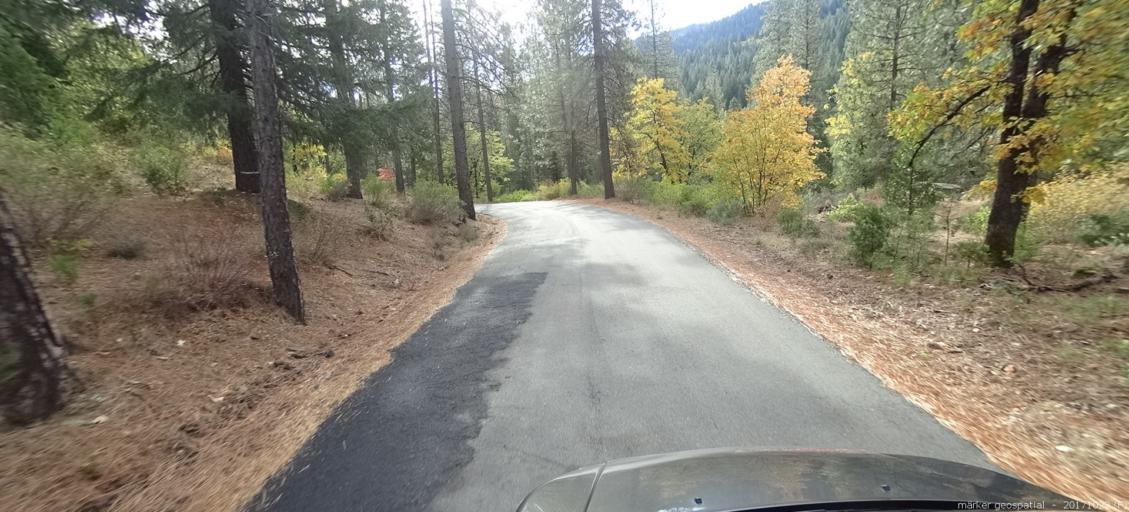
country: US
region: California
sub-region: Siskiyou County
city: Dunsmuir
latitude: 41.1560
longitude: -122.3607
